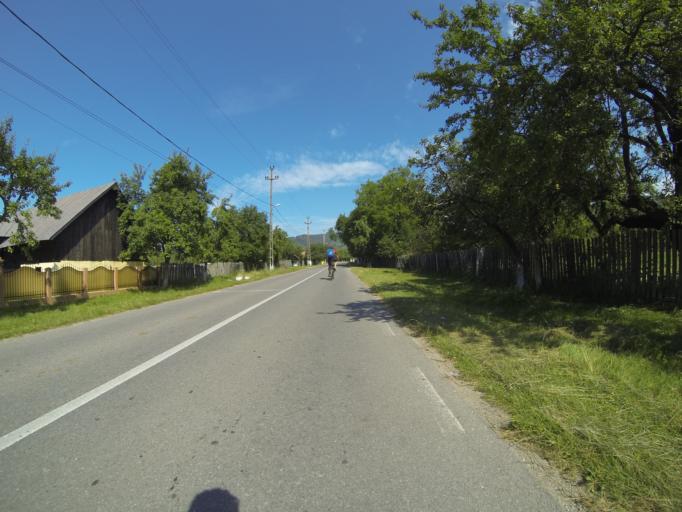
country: RO
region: Gorj
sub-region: Comuna Polovragi
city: Polovragi
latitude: 45.1776
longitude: 23.7966
